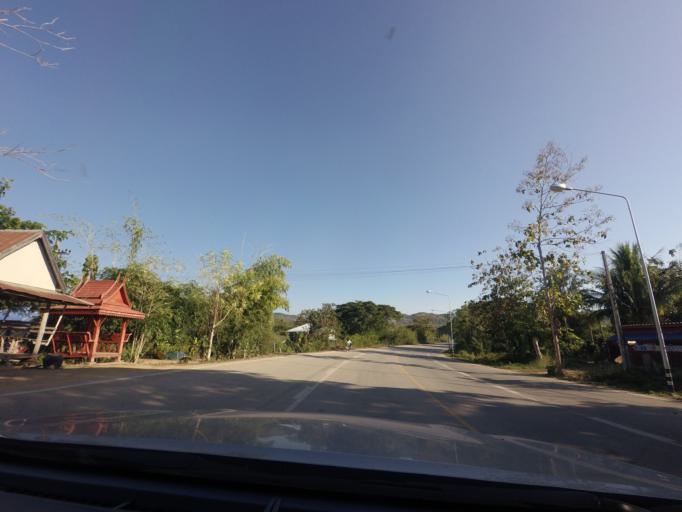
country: TH
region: Lampang
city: Chae Hom
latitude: 18.5137
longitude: 99.6425
